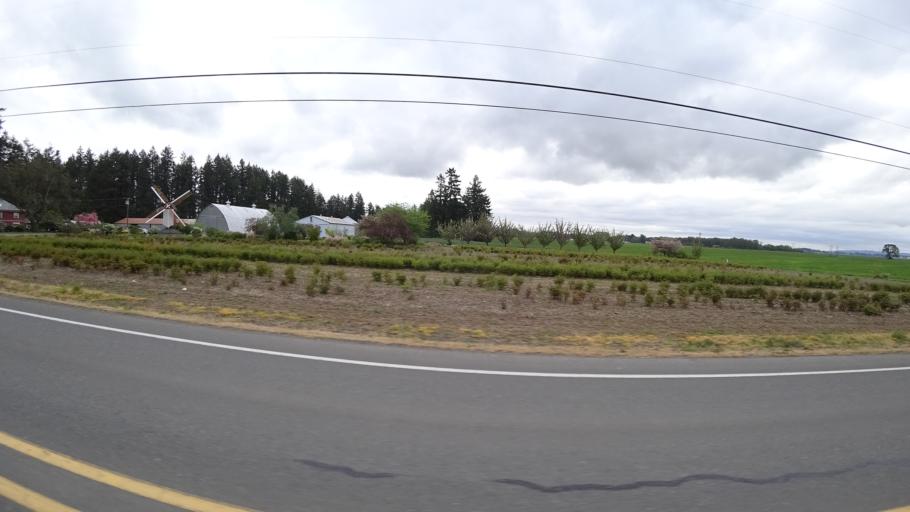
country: US
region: Oregon
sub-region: Washington County
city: North Plains
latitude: 45.5626
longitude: -122.9728
